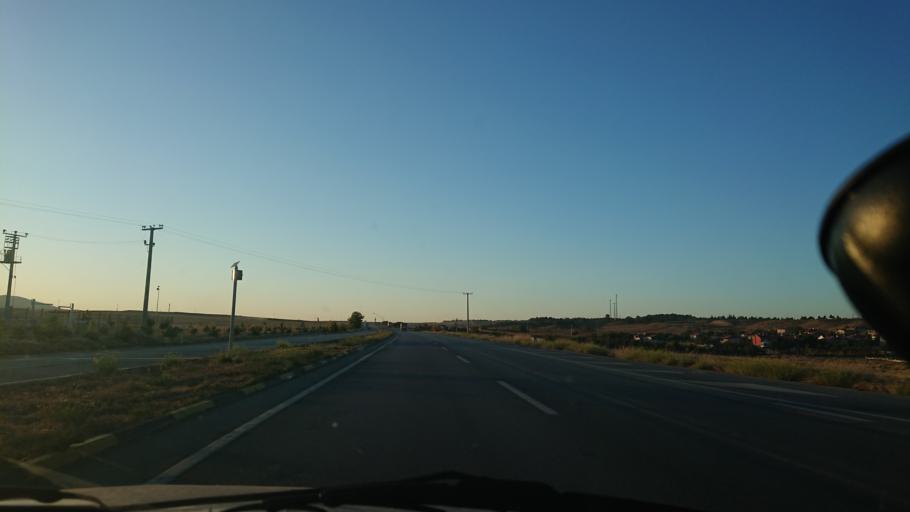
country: TR
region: Eskisehir
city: Mahmudiye
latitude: 39.4888
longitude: 30.9817
